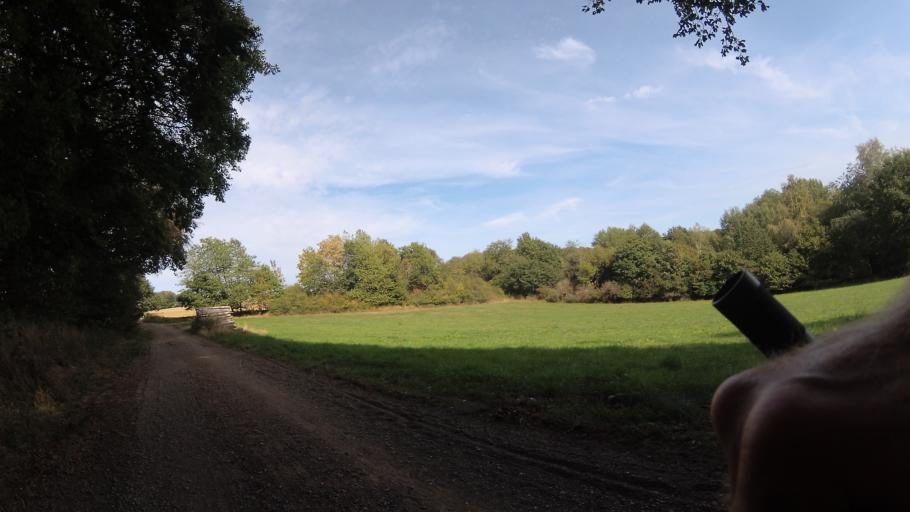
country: DE
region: Saarland
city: Sankt Wendel
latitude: 49.4826
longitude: 7.2024
